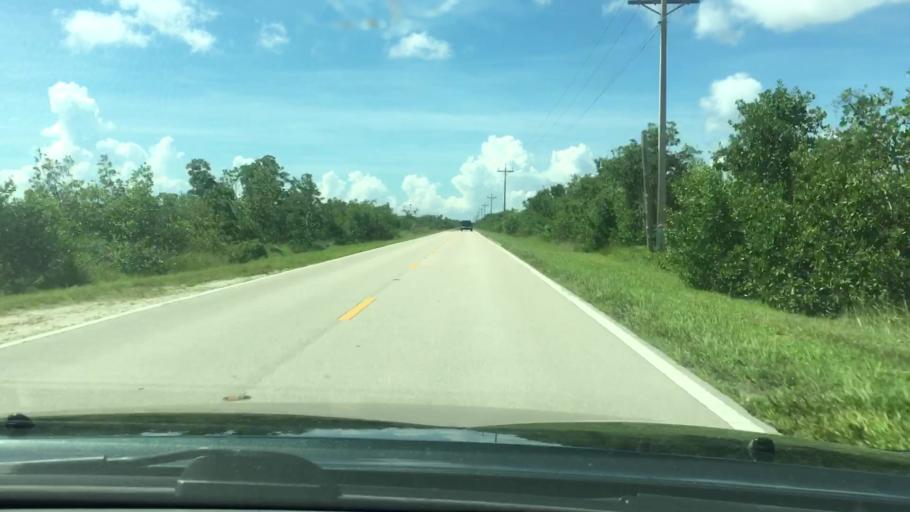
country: US
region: Florida
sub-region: Collier County
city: Marco
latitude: 25.9490
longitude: -81.6423
